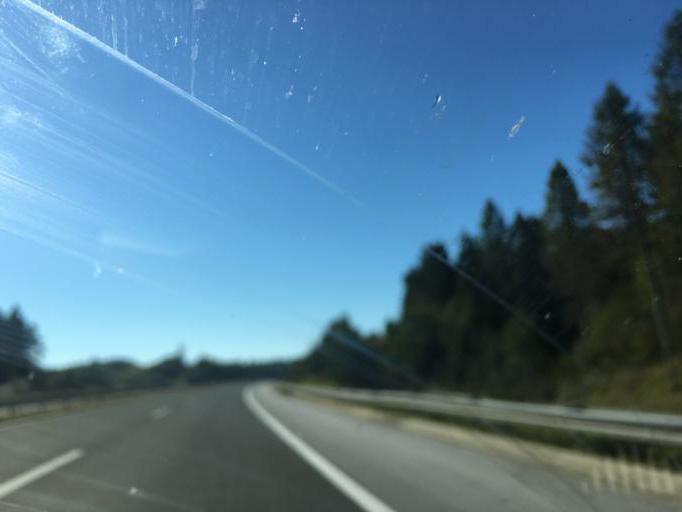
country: HR
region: Karlovacka
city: Ostarije
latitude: 45.2067
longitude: 15.2635
